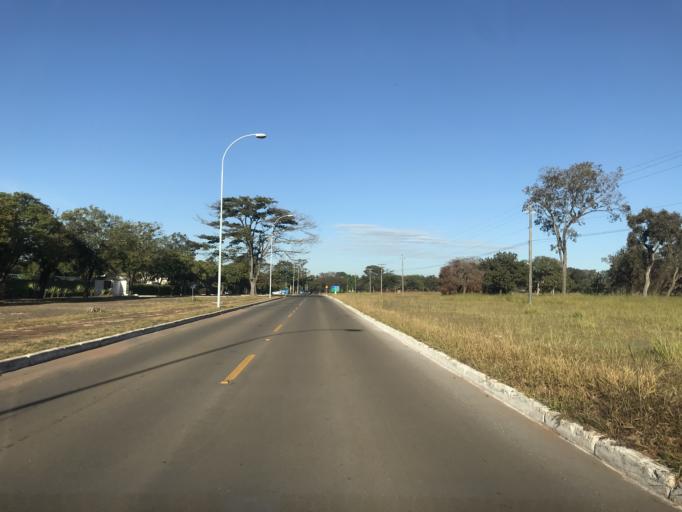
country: BR
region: Federal District
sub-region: Brasilia
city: Brasilia
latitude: -15.8297
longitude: -47.8973
